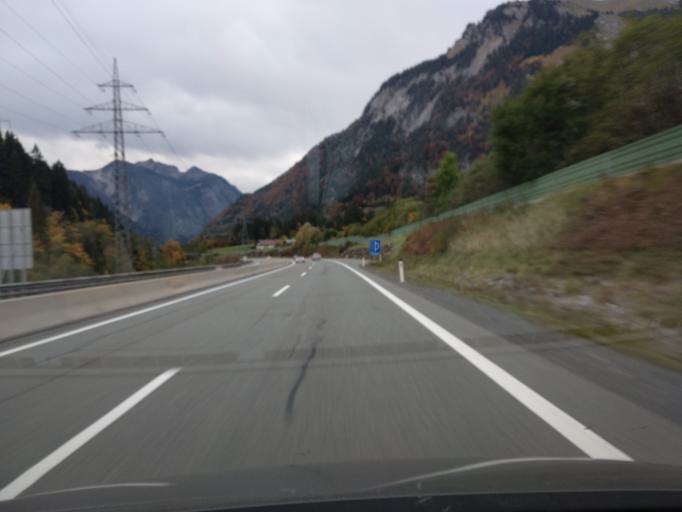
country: AT
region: Vorarlberg
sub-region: Politischer Bezirk Bludenz
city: Dalaas
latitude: 47.1279
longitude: 10.0359
